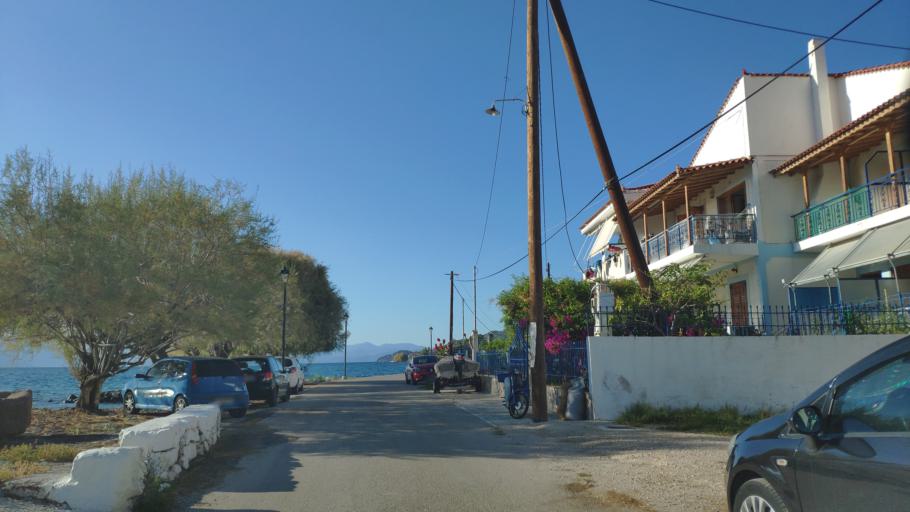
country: GR
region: Attica
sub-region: Nomos Piraios
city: Megalochori
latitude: 37.5871
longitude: 23.3471
